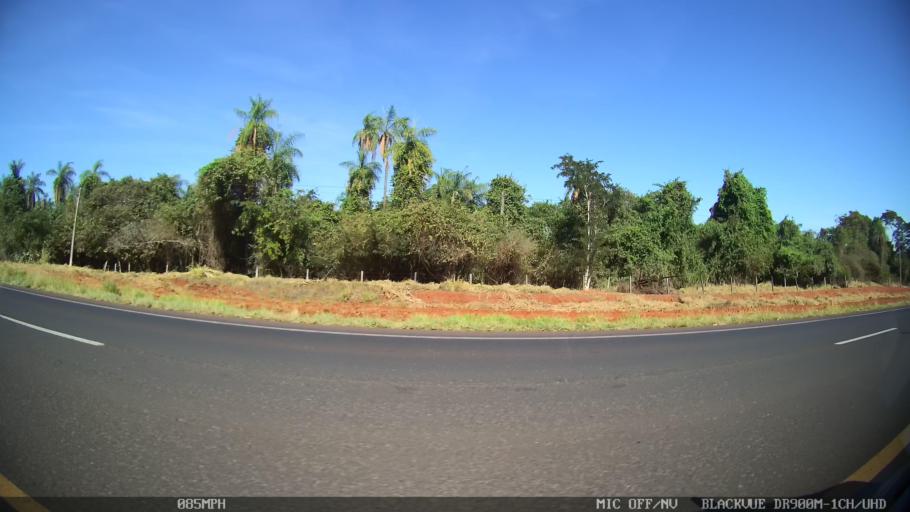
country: BR
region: Sao Paulo
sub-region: Barretos
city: Barretos
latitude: -20.5879
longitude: -48.7028
